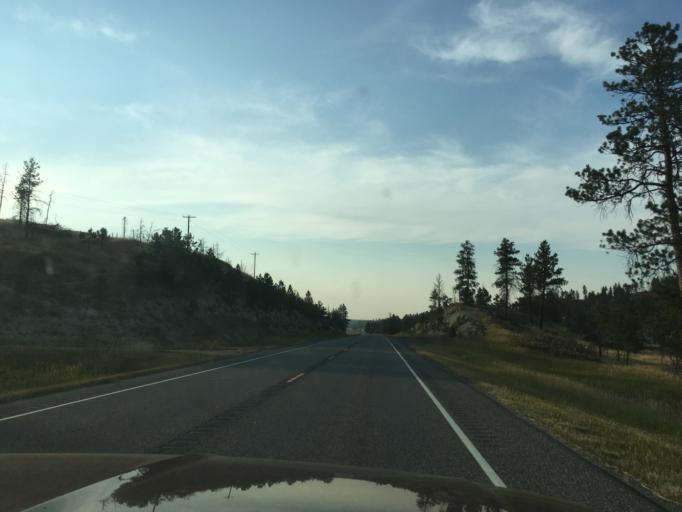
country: US
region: Montana
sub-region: Musselshell County
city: Roundup
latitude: 46.2761
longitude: -108.4740
